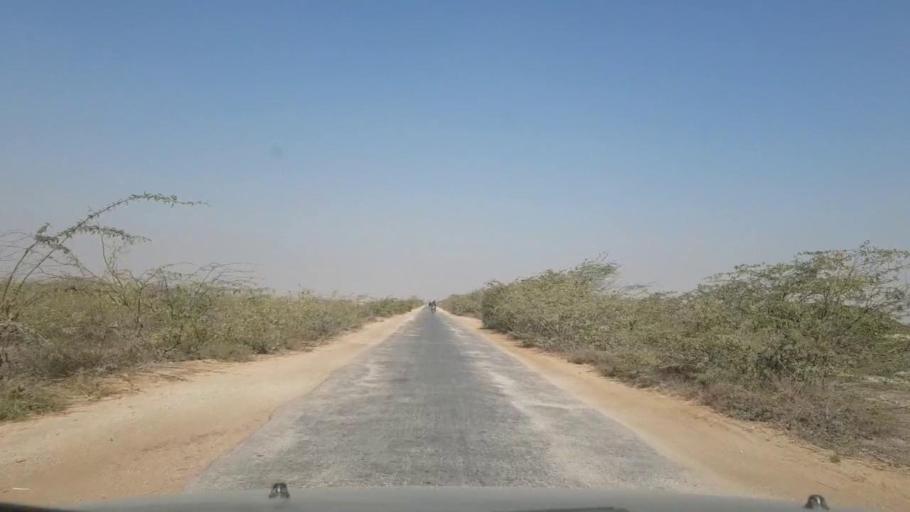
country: PK
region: Sindh
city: Thatta
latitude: 24.8301
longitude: 67.8918
